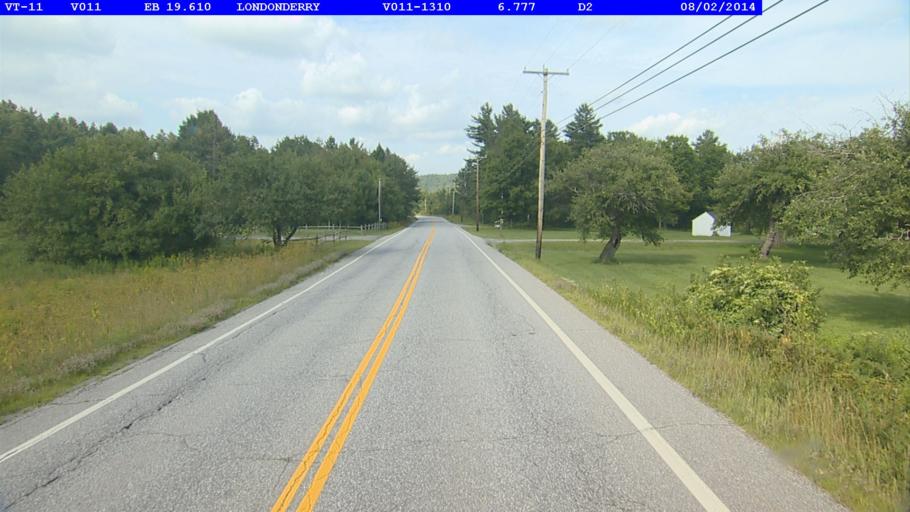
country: US
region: Vermont
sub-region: Windsor County
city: Chester
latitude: 43.2191
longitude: -72.7379
